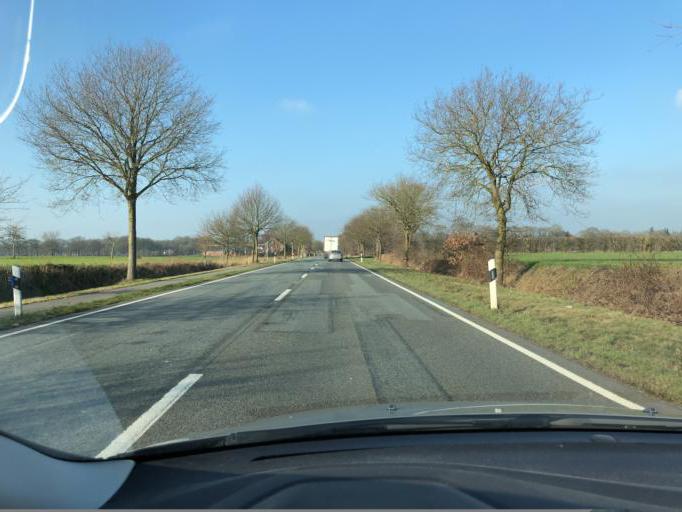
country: DE
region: Lower Saxony
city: Apen
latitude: 53.2972
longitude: 7.8168
